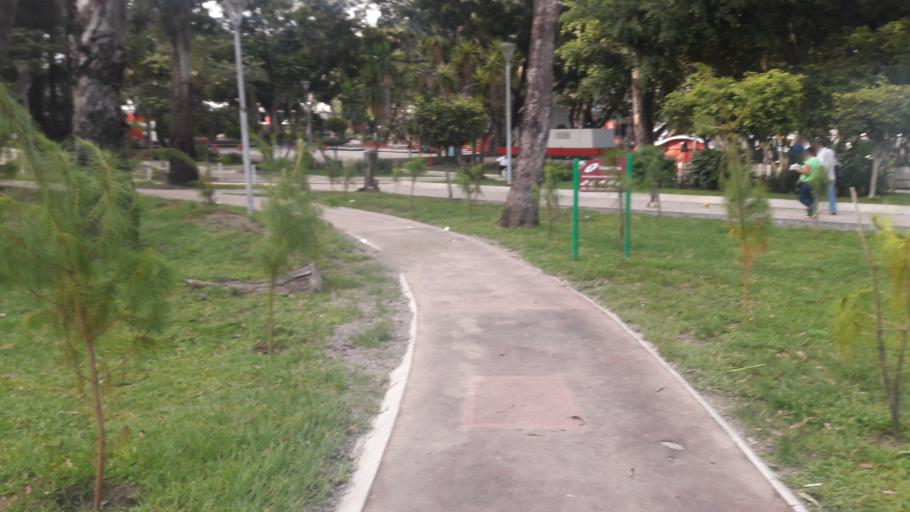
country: MX
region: Nayarit
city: Tepic
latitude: 21.5040
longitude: -104.8996
